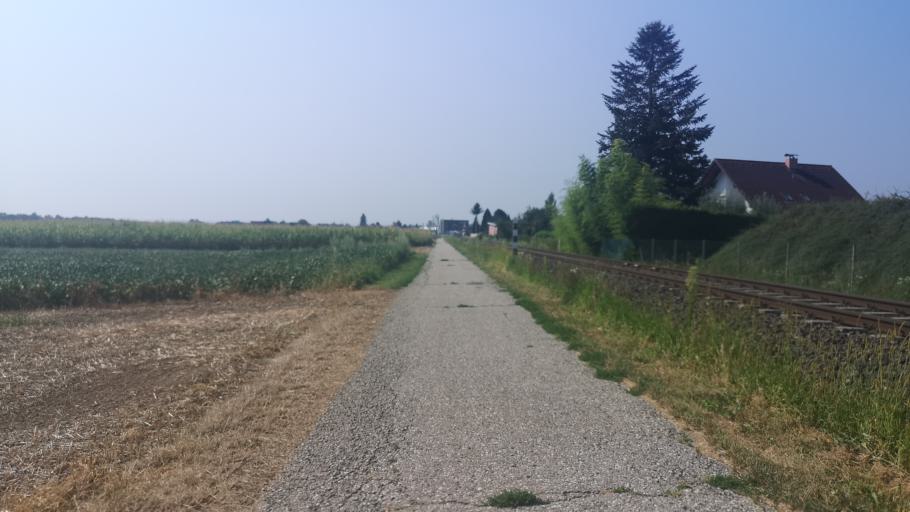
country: AT
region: Styria
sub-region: Politischer Bezirk Graz-Umgebung
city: Seiersberg
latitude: 47.0049
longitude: 15.4014
